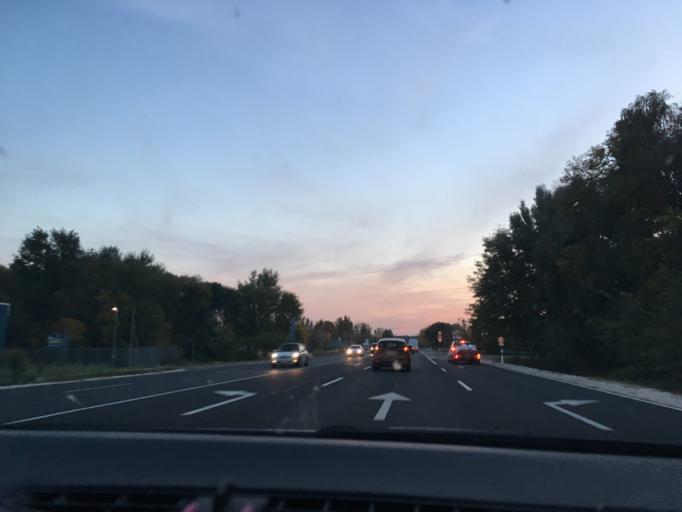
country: HU
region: Hajdu-Bihar
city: Debrecen
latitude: 47.6013
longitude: 21.6545
